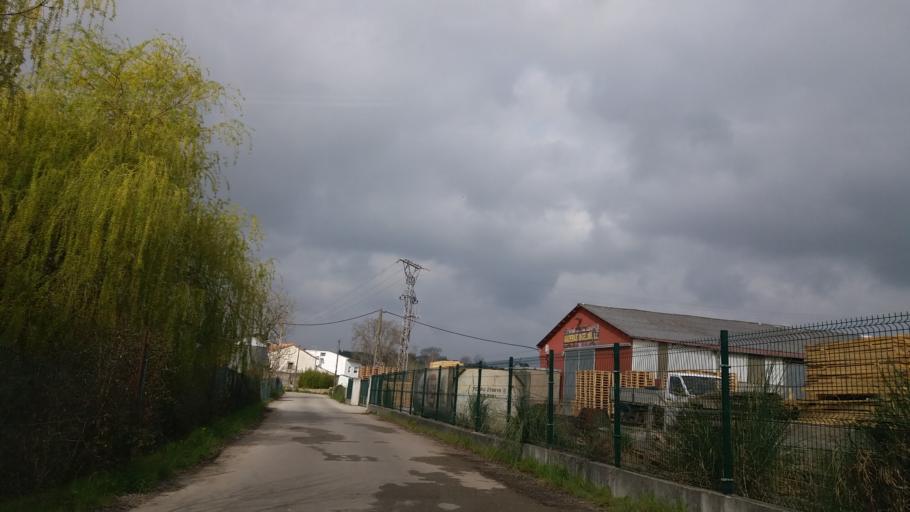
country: ES
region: Cantabria
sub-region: Provincia de Cantabria
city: Reocin
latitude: 43.3677
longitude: -4.0864
